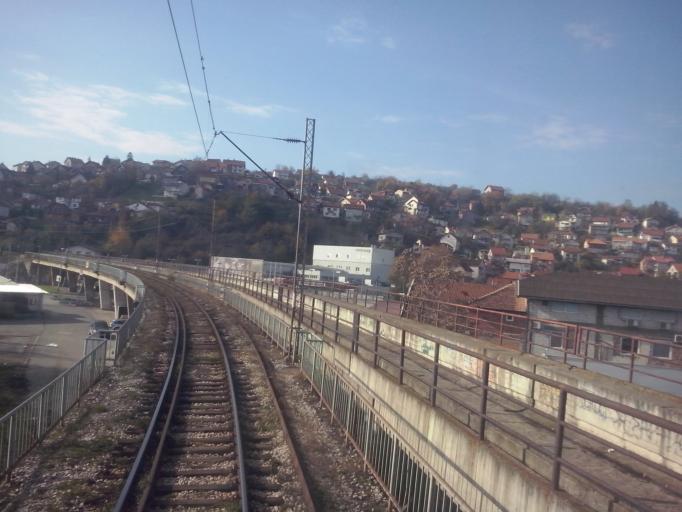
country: RS
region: Central Serbia
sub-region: Kolubarski Okrug
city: Valjevo
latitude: 44.2644
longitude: 19.8927
